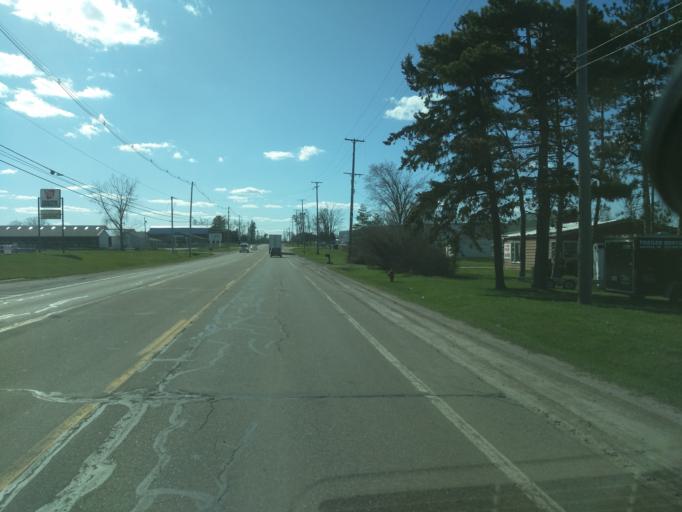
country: US
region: Michigan
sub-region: Eaton County
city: Waverly
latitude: 42.7765
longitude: -84.6261
